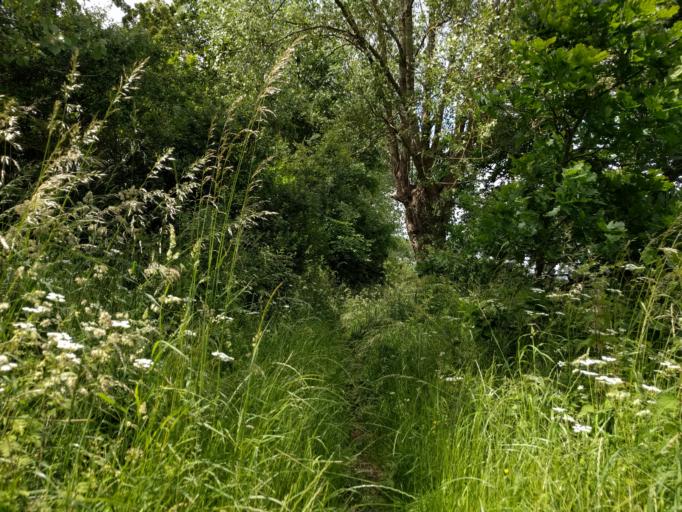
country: DK
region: South Denmark
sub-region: Odense Kommune
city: Bullerup
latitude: 55.4297
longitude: 10.4919
